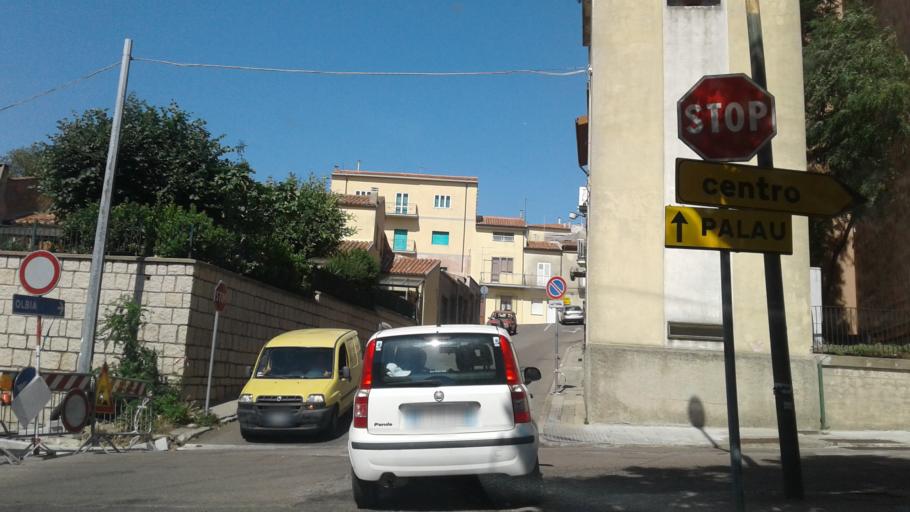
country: IT
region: Sardinia
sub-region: Provincia di Olbia-Tempio
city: Tempio Pausania
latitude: 40.9051
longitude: 9.1003
